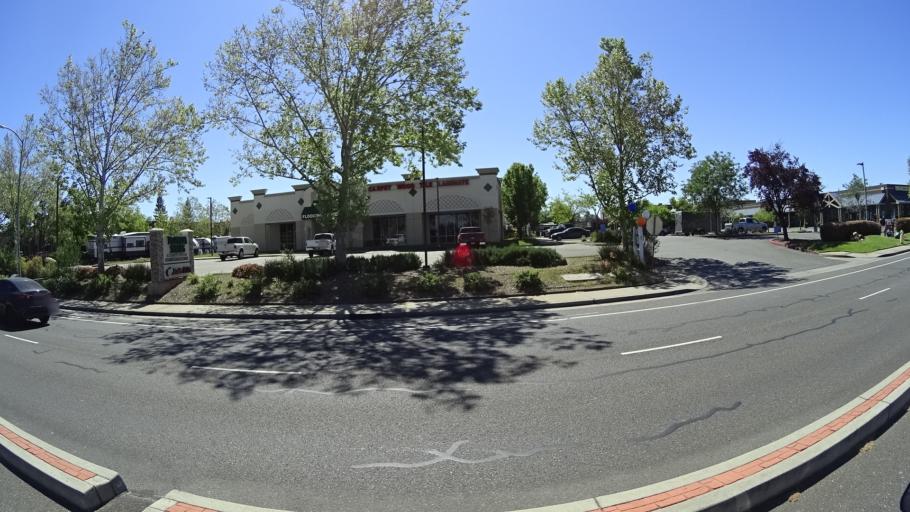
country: US
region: California
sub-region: Placer County
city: Rocklin
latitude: 38.7984
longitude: -121.2141
